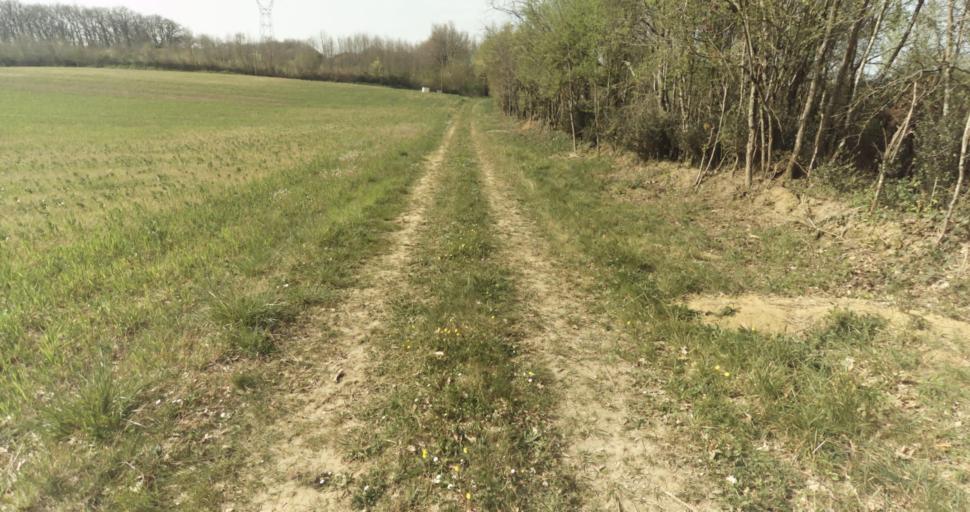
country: FR
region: Midi-Pyrenees
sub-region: Departement du Tarn-et-Garonne
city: Lafrancaise
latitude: 44.1347
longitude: 1.1720
